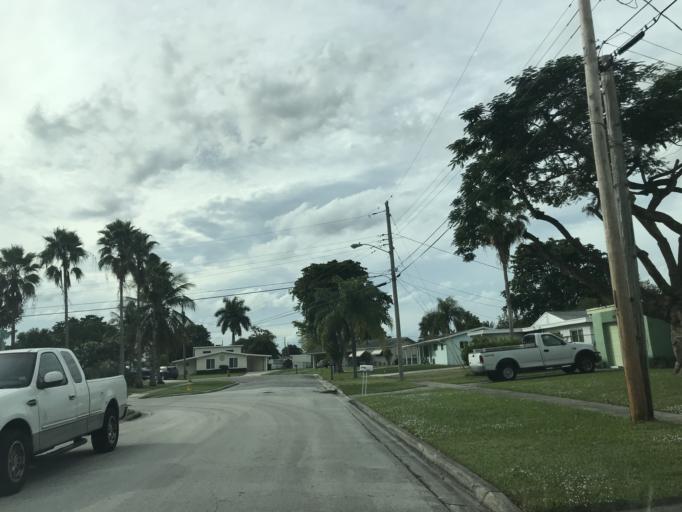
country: US
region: Florida
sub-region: Broward County
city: Margate
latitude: 26.2567
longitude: -80.2078
